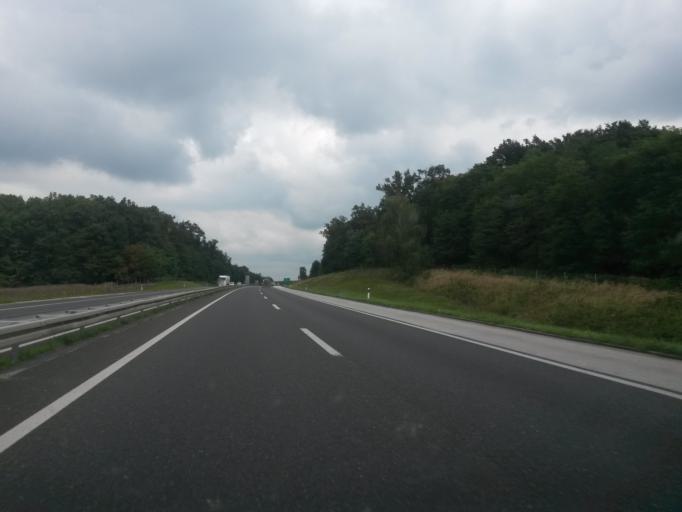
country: HR
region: Grad Zagreb
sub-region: Sesvete
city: Sesvete
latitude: 45.8336
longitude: 16.1374
